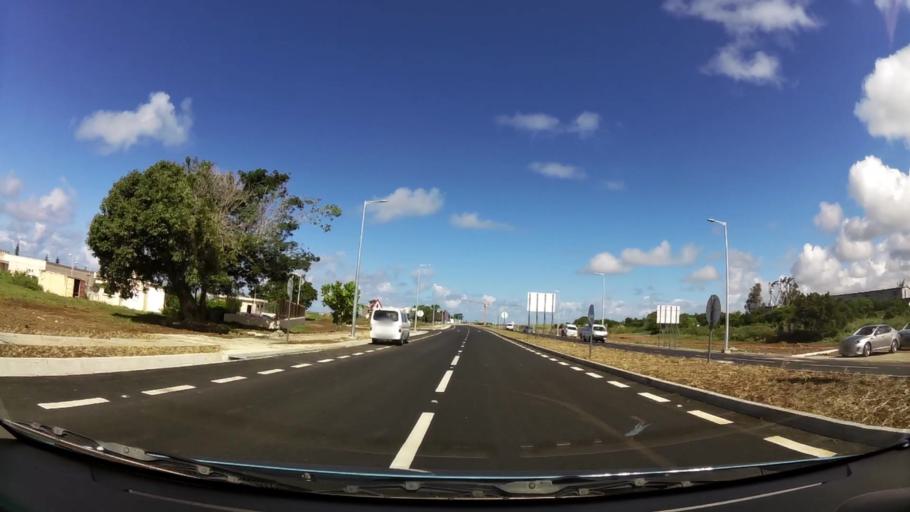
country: MU
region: Grand Port
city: Plaine Magnien
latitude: -20.4357
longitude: 57.6734
